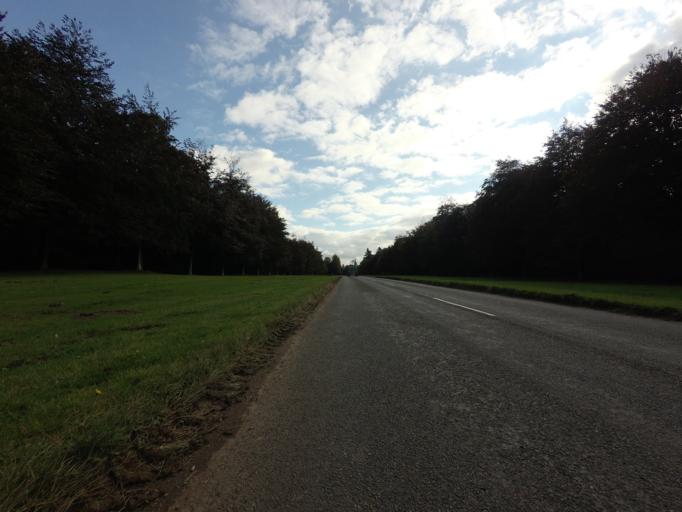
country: GB
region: England
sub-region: Norfolk
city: Dersingham
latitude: 52.8357
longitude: 0.5116
